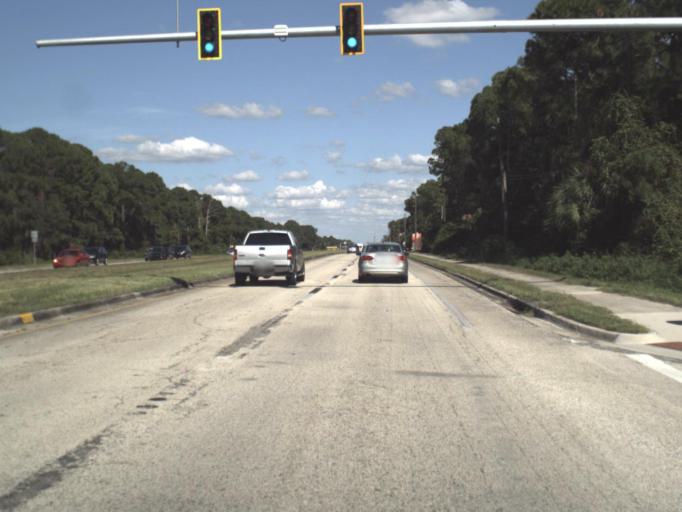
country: US
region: Florida
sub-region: Sarasota County
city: North Port
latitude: 27.0038
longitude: -82.1723
